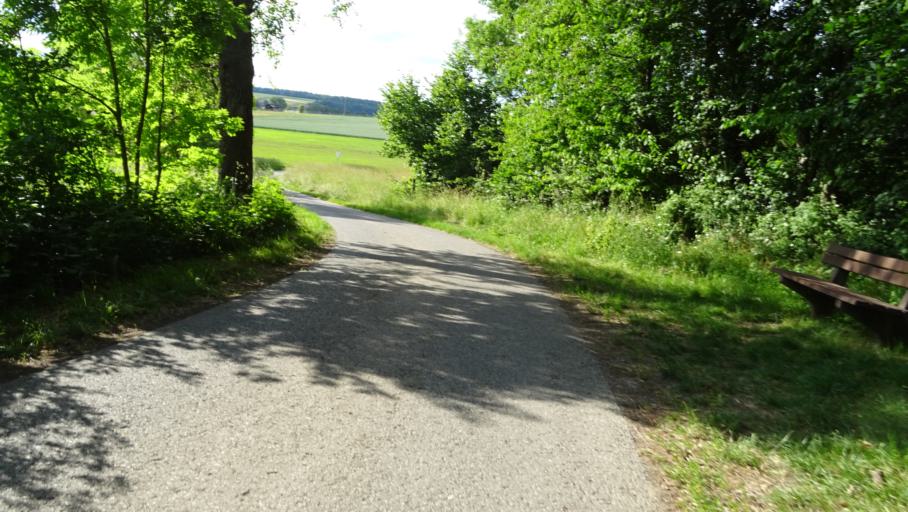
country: DE
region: Baden-Wuerttemberg
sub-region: Regierungsbezirk Stuttgart
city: Offenau
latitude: 49.2545
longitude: 9.1688
